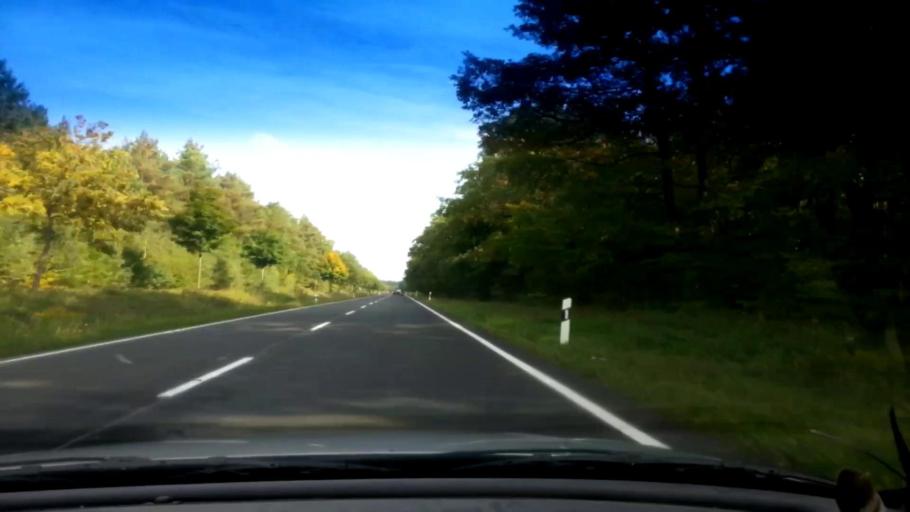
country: DE
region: Bavaria
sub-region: Upper Franconia
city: Bamberg
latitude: 49.8892
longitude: 10.9335
